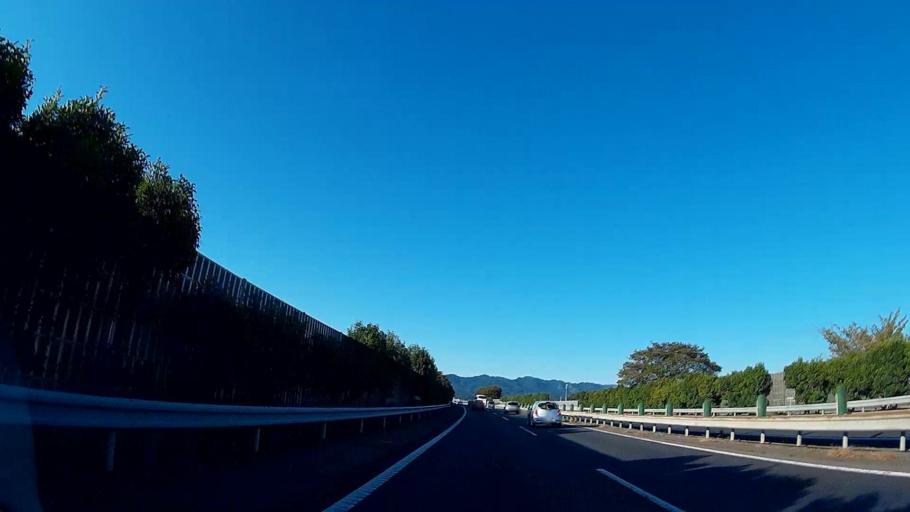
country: JP
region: Tokyo
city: Hachioji
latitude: 35.6758
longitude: 139.3144
